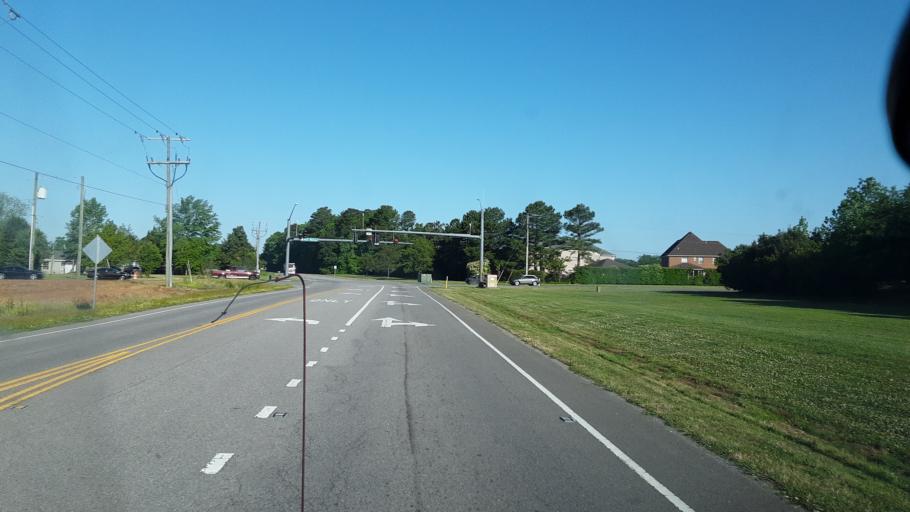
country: US
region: Virginia
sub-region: City of Virginia Beach
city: Virginia Beach
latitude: 36.7219
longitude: -76.0505
